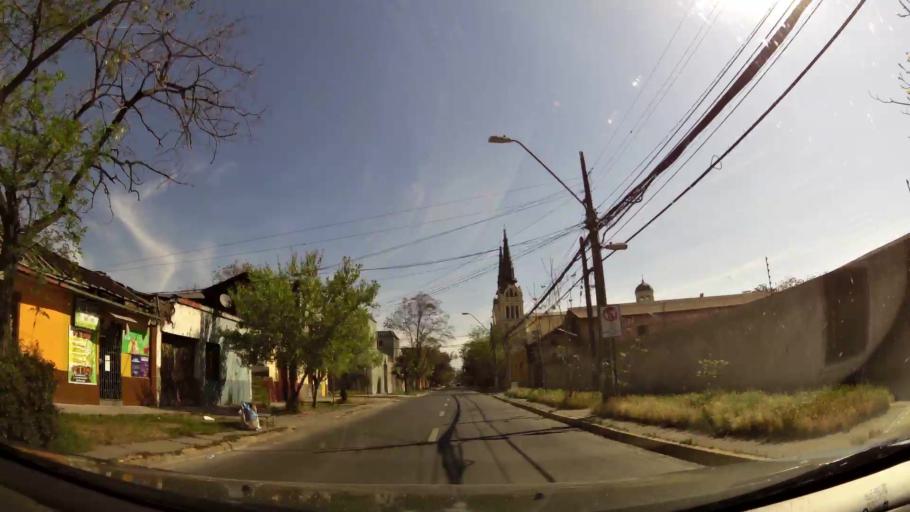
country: CL
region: Santiago Metropolitan
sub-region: Provincia de Santiago
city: Santiago
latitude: -33.4264
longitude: -70.6592
